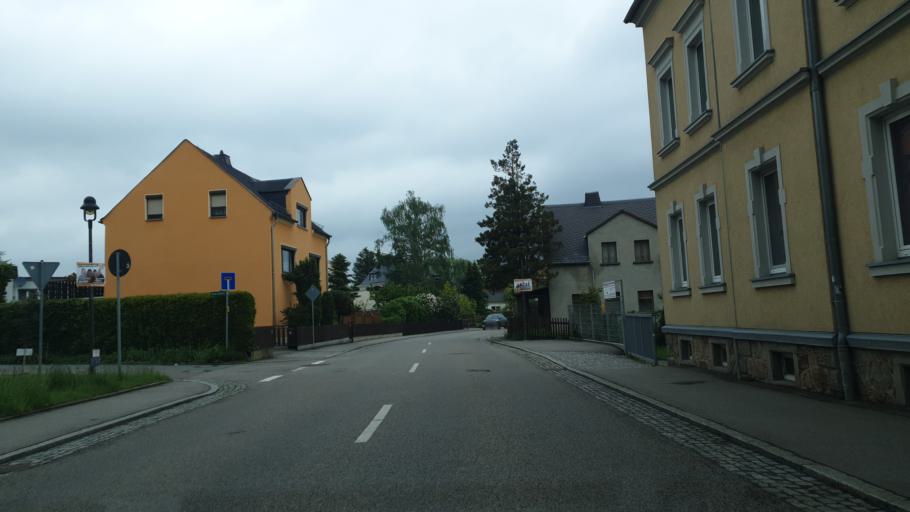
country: DE
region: Saxony
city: Limbach-Oberfrohna
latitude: 50.8577
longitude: 12.7964
